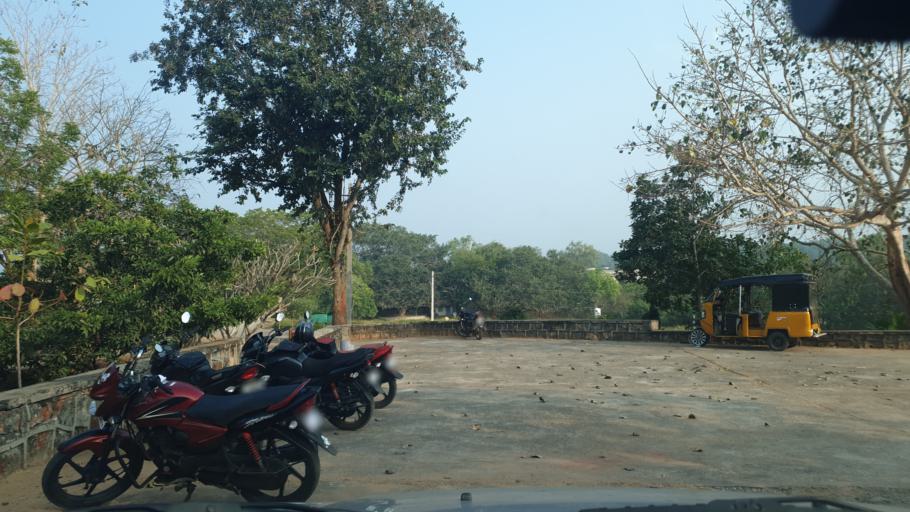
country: IN
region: Andhra Pradesh
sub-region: Srikakulam
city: Narasannapeta
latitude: 18.3335
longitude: 84.0462
